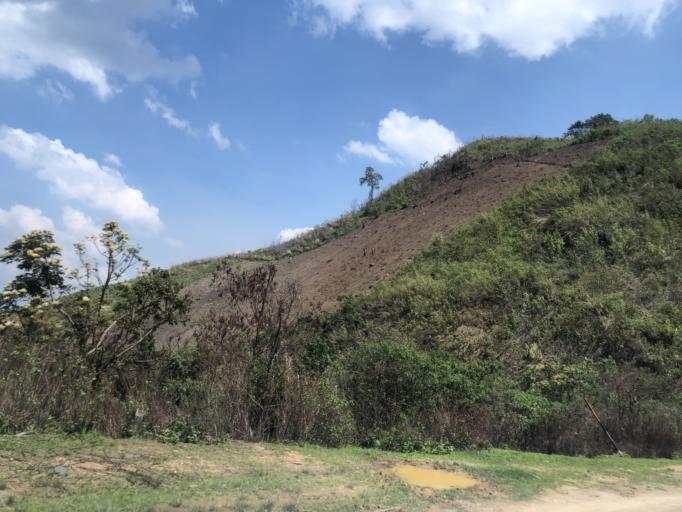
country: LA
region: Phongsali
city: Phongsali
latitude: 21.3973
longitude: 102.2142
